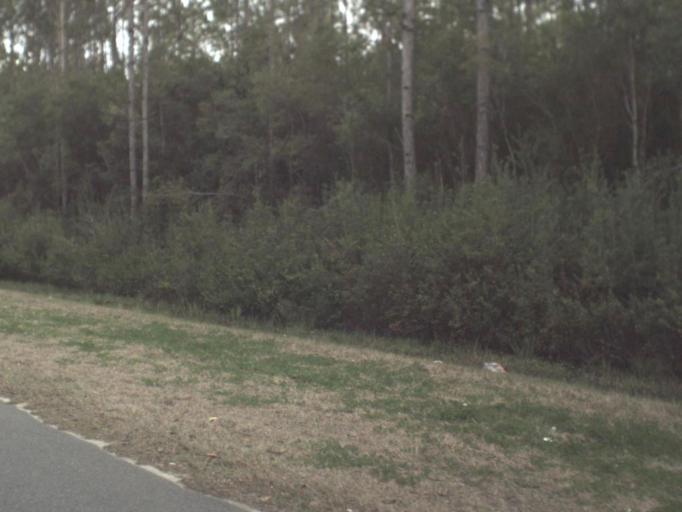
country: US
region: Florida
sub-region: Bay County
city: Callaway
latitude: 30.1527
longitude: -85.5311
